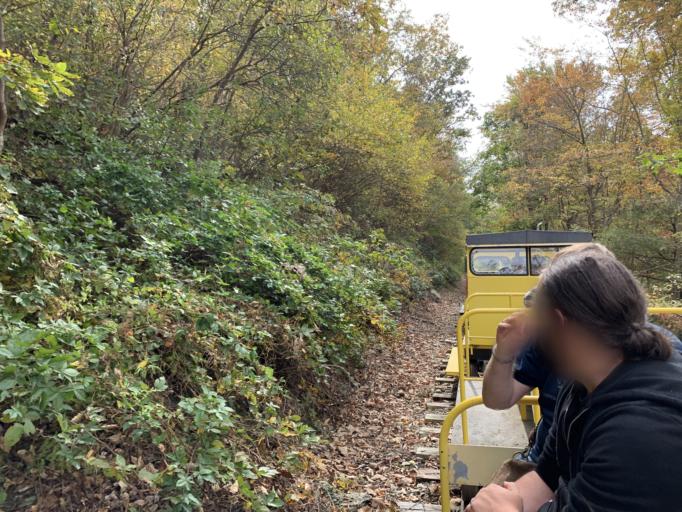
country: US
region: Pennsylvania
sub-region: York County
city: Susquehanna Trails
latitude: 39.8114
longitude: -76.4758
